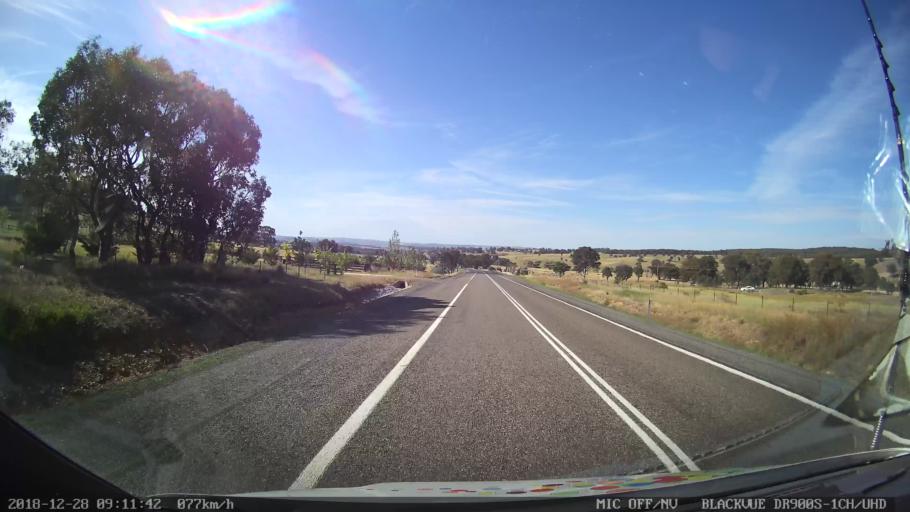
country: AU
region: New South Wales
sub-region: Upper Lachlan Shire
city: Crookwell
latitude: -34.2465
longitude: 149.3386
